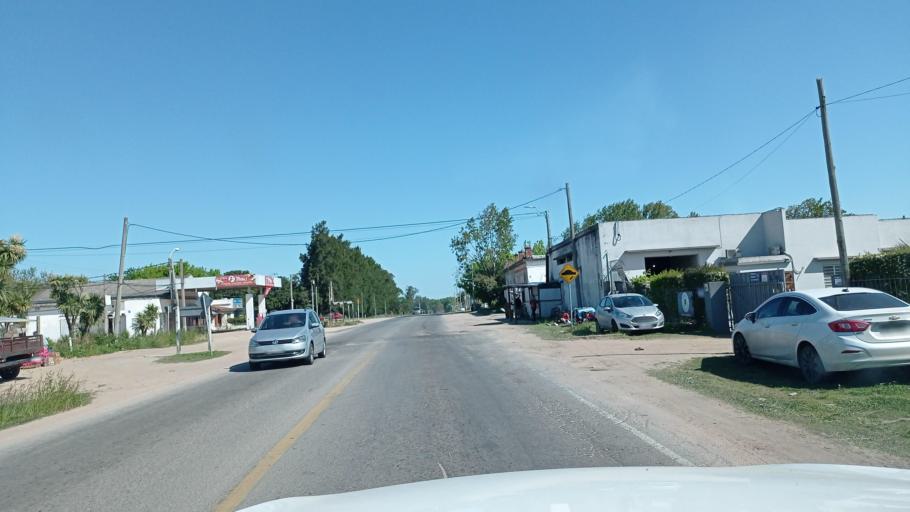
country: UY
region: Canelones
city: La Paz
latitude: -34.7897
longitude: -56.1658
